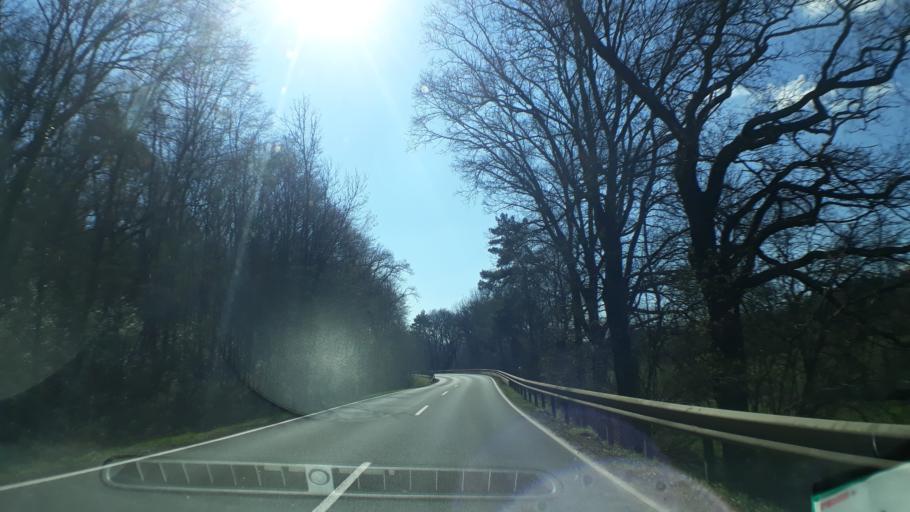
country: DE
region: North Rhine-Westphalia
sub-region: Regierungsbezirk Koln
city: Mechernich
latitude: 50.5985
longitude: 6.6806
